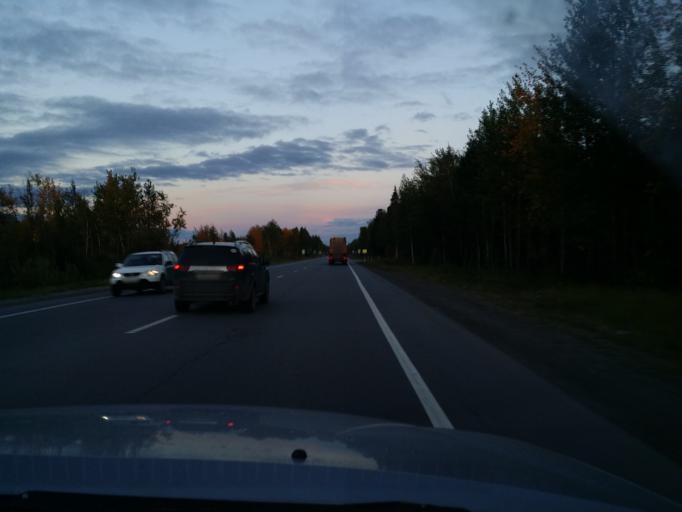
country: RU
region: Khanty-Mansiyskiy Avtonomnyy Okrug
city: Megion
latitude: 61.0661
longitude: 76.2590
